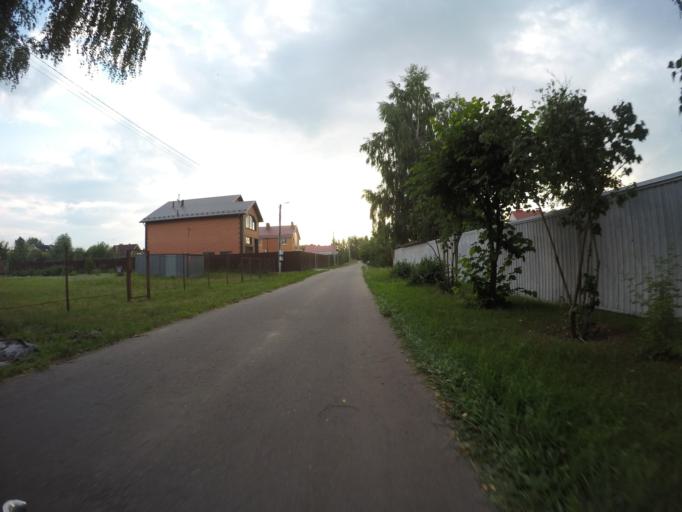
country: RU
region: Moskovskaya
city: Rechitsy
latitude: 55.5927
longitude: 38.5064
